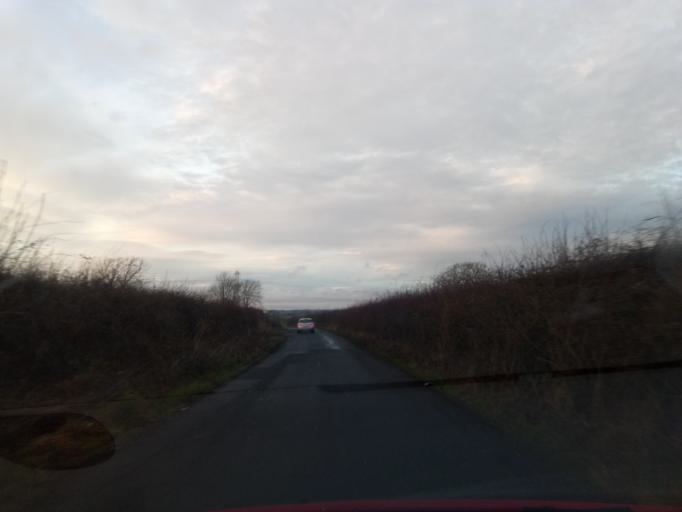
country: GB
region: England
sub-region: Northumberland
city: Ponteland
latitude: 55.0759
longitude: -1.7354
